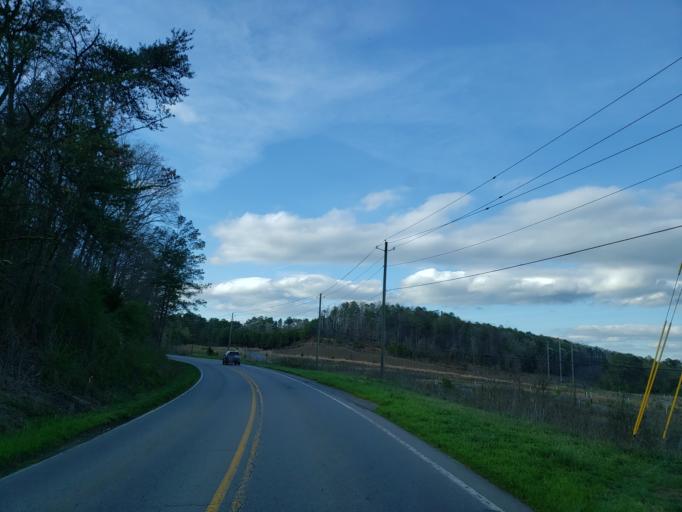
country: US
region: Georgia
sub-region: Bartow County
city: Cartersville
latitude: 34.2282
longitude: -84.8181
